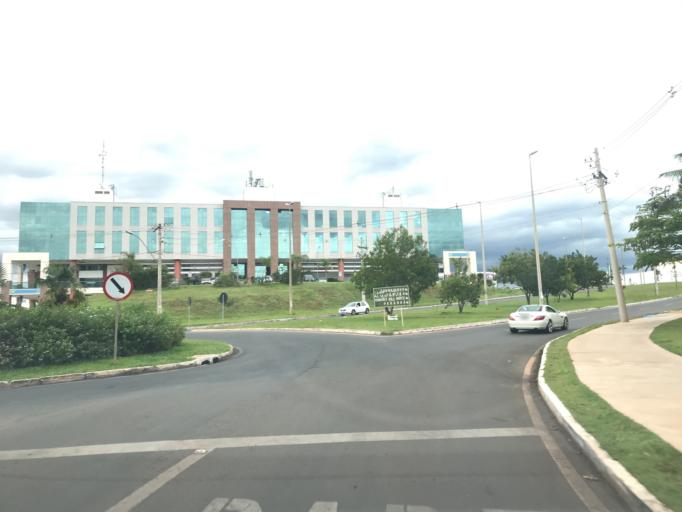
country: BR
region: Federal District
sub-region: Brasilia
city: Brasilia
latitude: -15.7205
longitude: -47.8806
